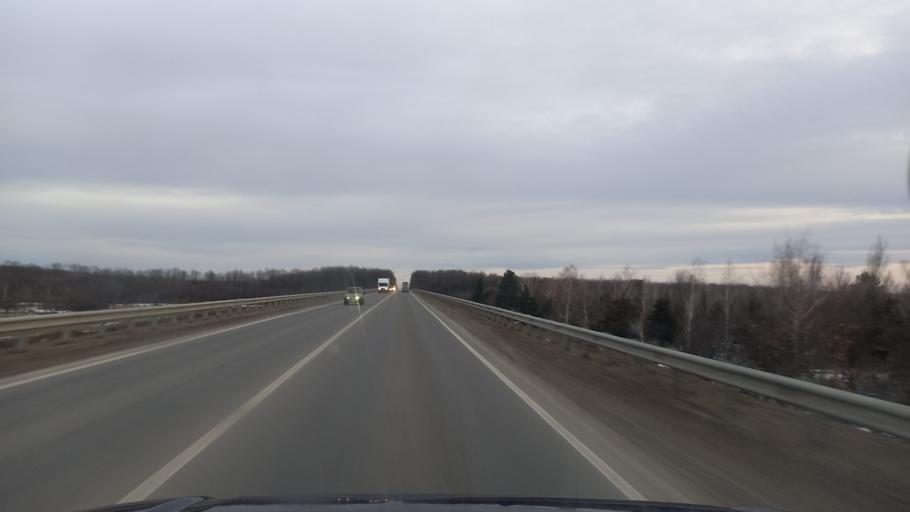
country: RU
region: Krasnodarskiy
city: Belorechensk
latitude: 44.7646
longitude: 39.9136
